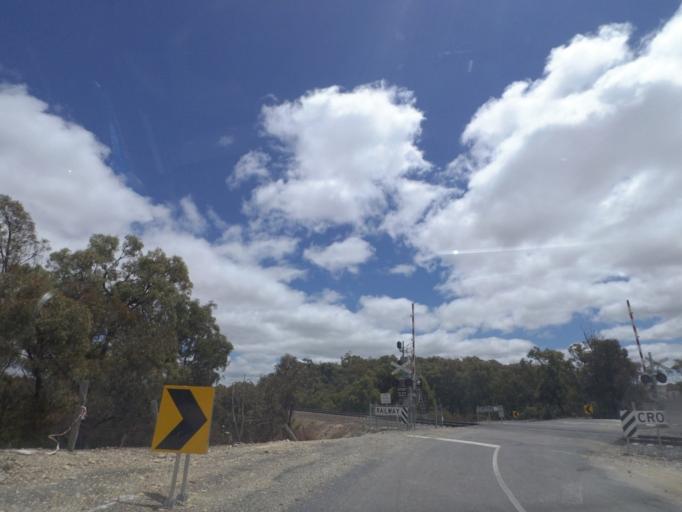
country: AU
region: Victoria
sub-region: Moorabool
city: Bacchus Marsh
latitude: -37.6670
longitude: 144.3382
